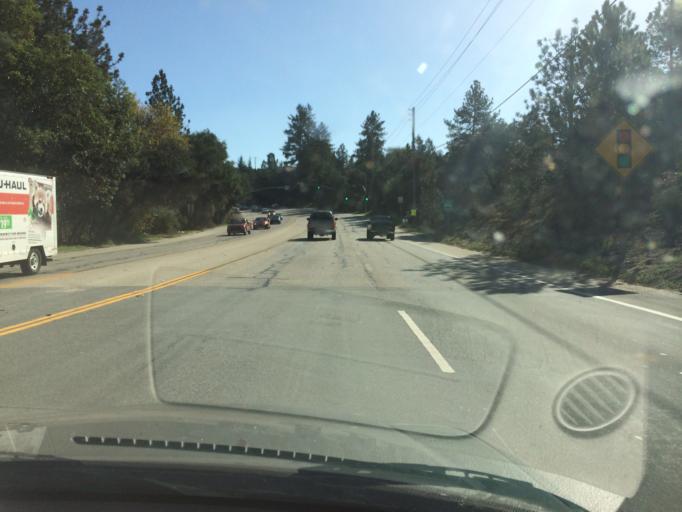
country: US
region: California
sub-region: Santa Cruz County
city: Mount Hermon
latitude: 37.0517
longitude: -122.0378
